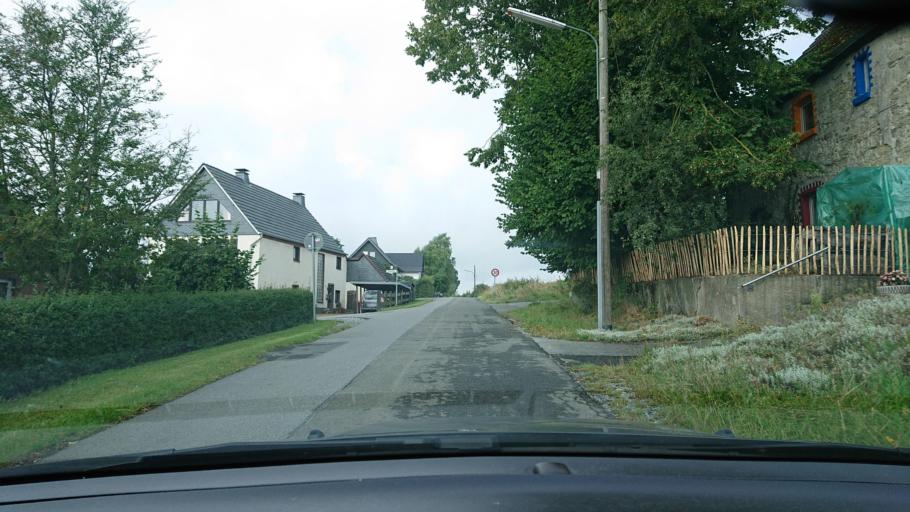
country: DE
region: North Rhine-Westphalia
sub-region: Regierungsbezirk Arnsberg
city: Anrochte
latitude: 51.5034
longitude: 8.2802
